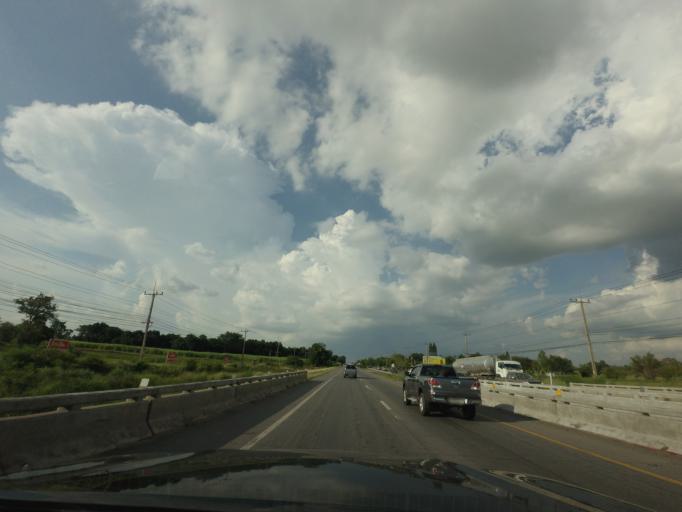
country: TH
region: Khon Kaen
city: Ban Haet
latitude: 16.2396
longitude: 102.7697
